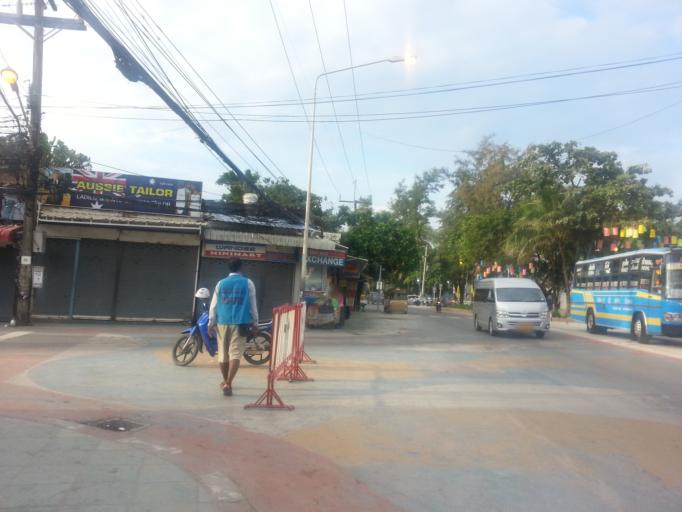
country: TH
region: Phuket
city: Patong
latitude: 7.8941
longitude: 98.2954
